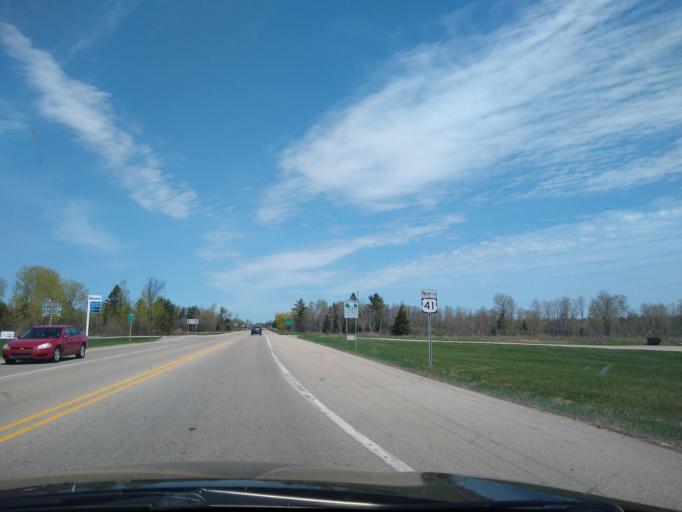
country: US
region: Michigan
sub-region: Delta County
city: Gladstone
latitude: 45.9271
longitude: -86.9747
